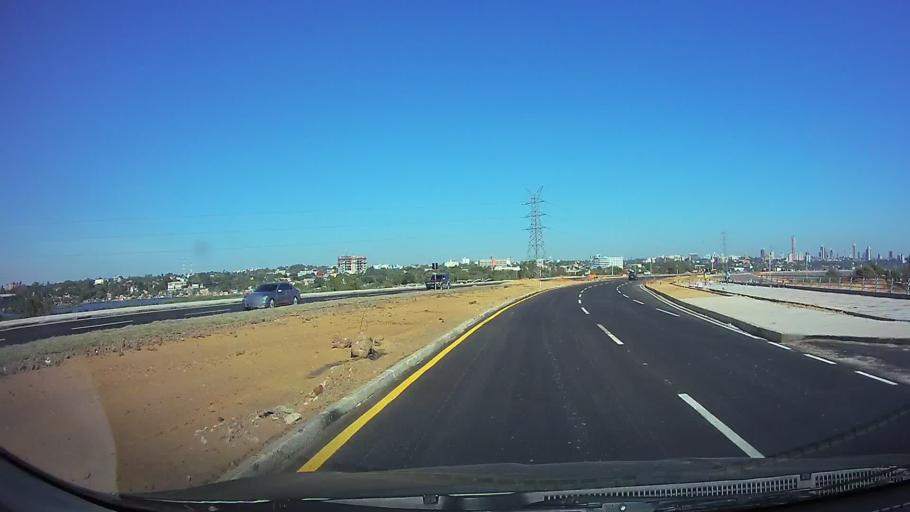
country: PY
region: Asuncion
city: Asuncion
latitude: -25.2609
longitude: -57.6071
